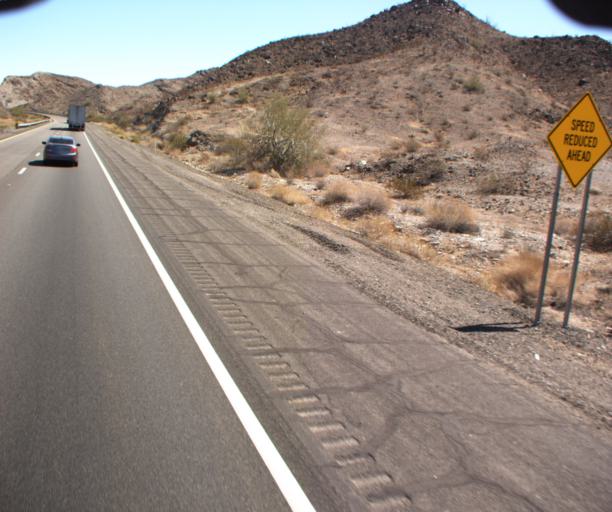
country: US
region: Arizona
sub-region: Yuma County
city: Fortuna Foothills
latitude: 32.6584
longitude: -114.3389
